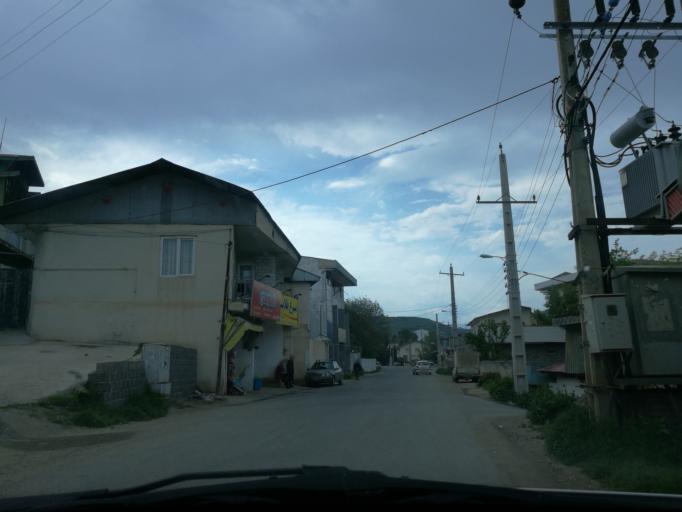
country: IR
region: Mazandaran
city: Chalus
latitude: 36.5299
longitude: 51.2294
